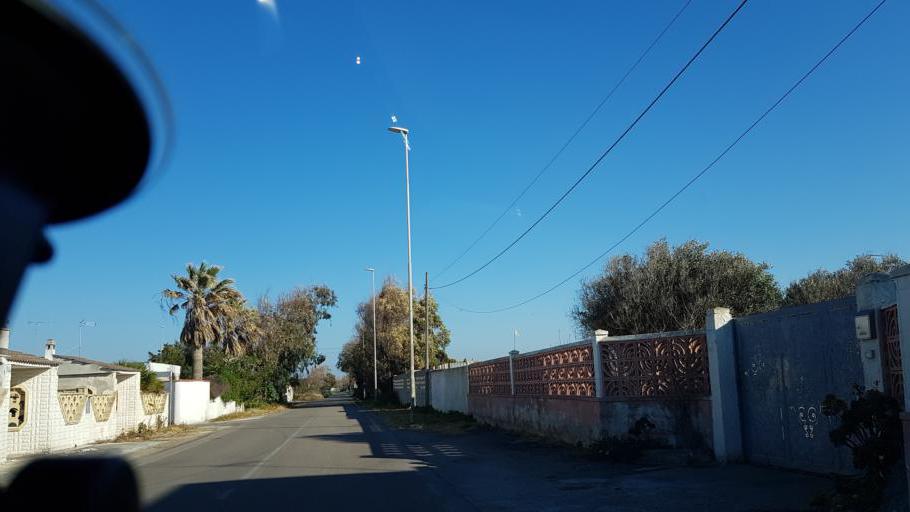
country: IT
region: Apulia
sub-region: Provincia di Lecce
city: Giorgilorio
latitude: 40.4523
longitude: 18.2191
